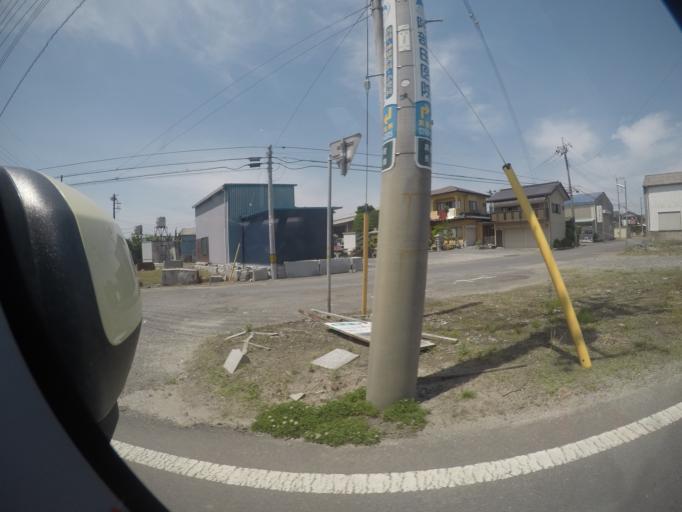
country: JP
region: Ibaraki
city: Makabe
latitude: 36.2913
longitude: 140.1103
